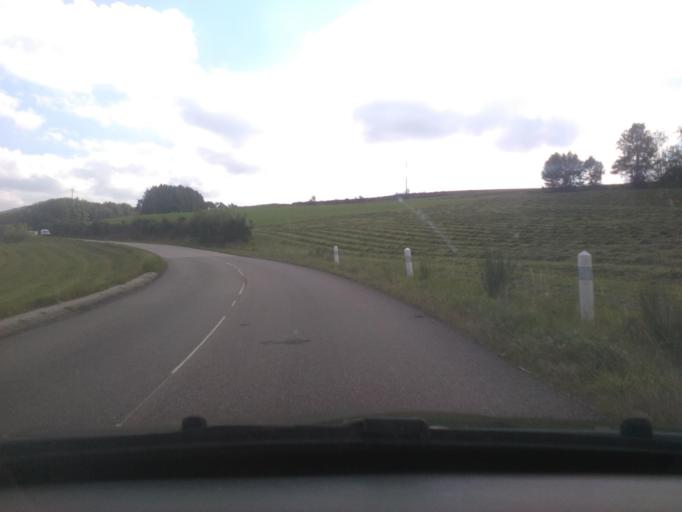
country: FR
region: Lorraine
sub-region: Departement des Vosges
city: Corcieux
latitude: 48.1537
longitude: 6.8619
